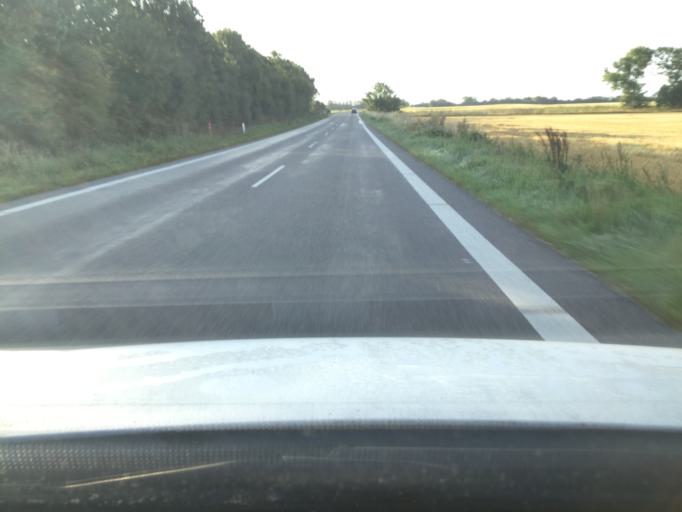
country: DK
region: Zealand
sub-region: Lolland Kommune
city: Rodby
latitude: 54.7878
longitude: 11.2865
